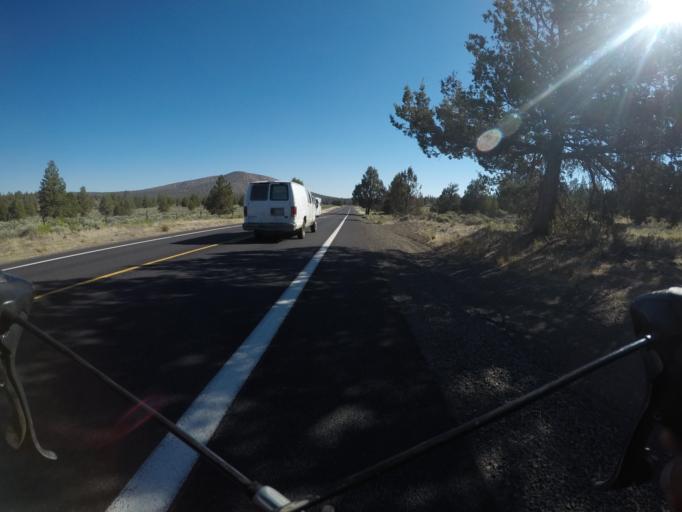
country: US
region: Oregon
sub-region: Deschutes County
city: Redmond
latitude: 44.2269
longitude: -121.3078
